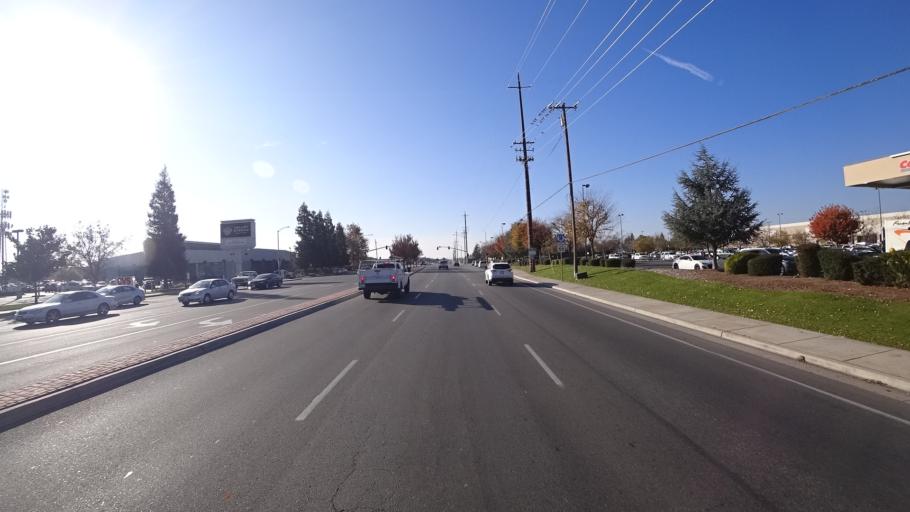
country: US
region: California
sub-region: Kern County
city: Greenfield
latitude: 35.2960
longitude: -119.0571
